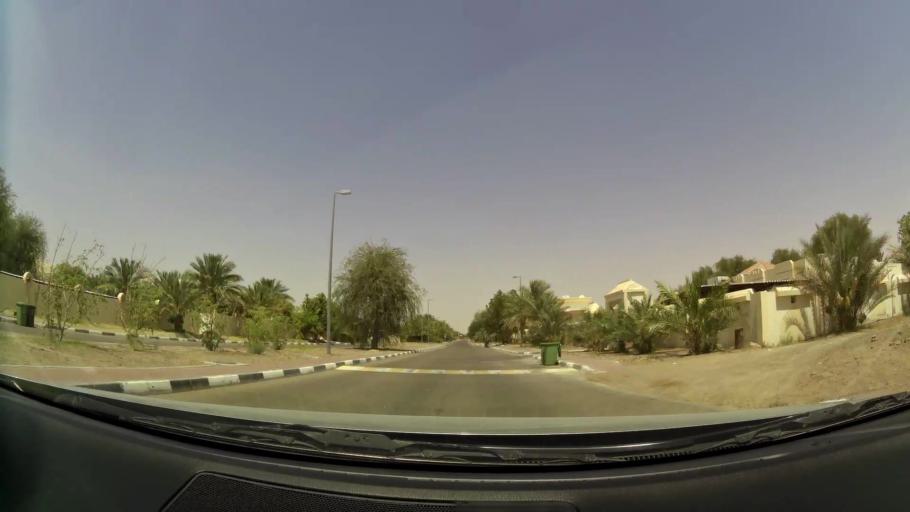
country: OM
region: Al Buraimi
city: Al Buraymi
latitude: 24.2853
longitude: 55.7584
